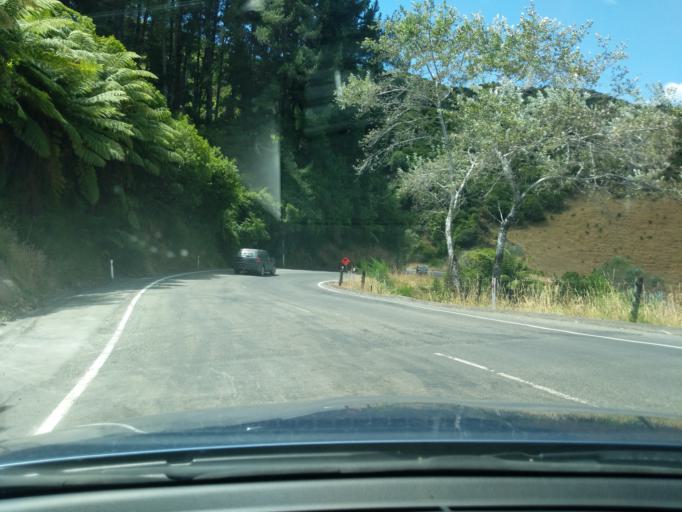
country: NZ
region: Tasman
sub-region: Tasman District
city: Motueka
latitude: -41.0492
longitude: 172.9593
